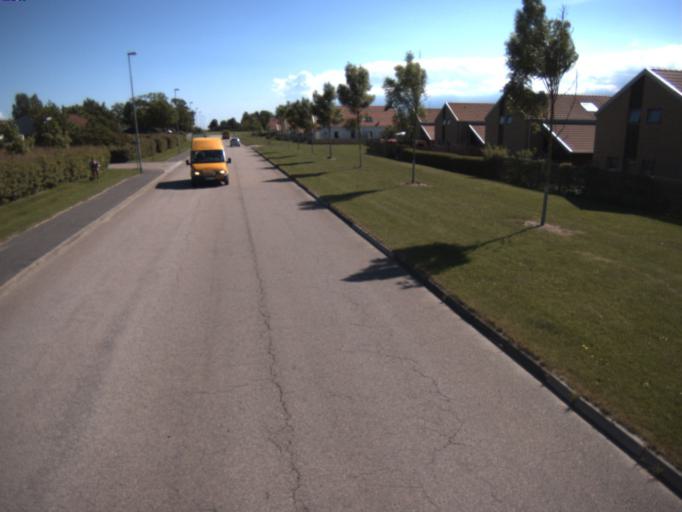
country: SE
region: Skane
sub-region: Helsingborg
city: Rydeback
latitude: 55.9602
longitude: 12.7652
